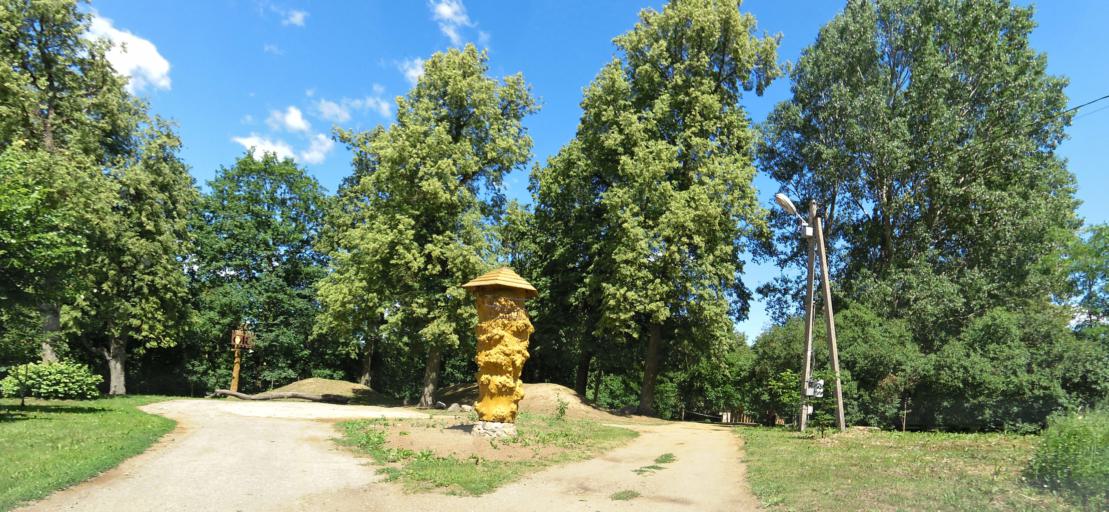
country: LT
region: Panevezys
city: Pasvalys
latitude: 56.2302
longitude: 24.4168
